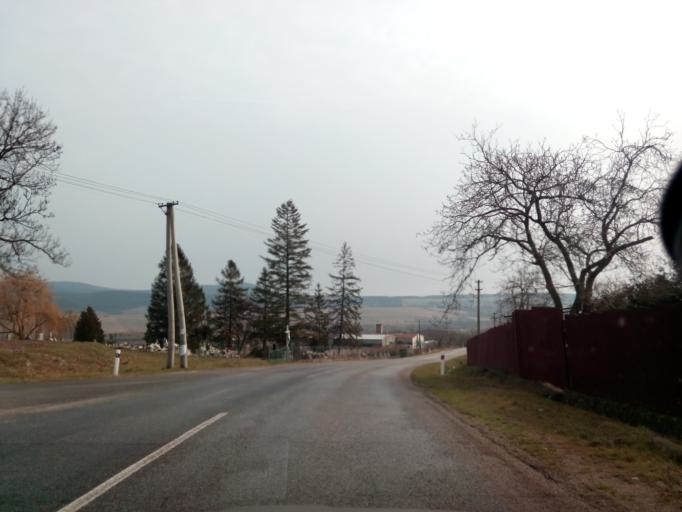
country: SK
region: Kosicky
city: Secovce
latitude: 48.6370
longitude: 21.4814
